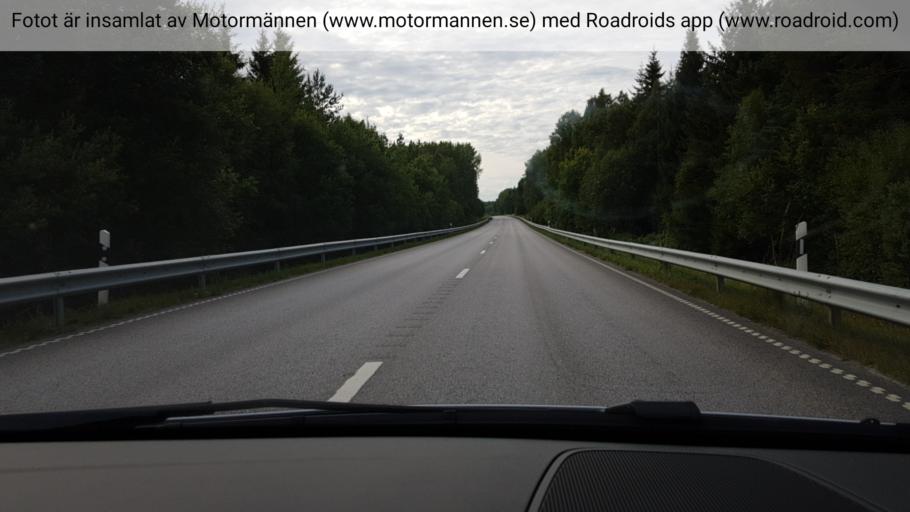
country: SE
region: Stockholm
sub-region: Norrtalje Kommun
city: Skanninge
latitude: 59.8949
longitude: 18.6224
